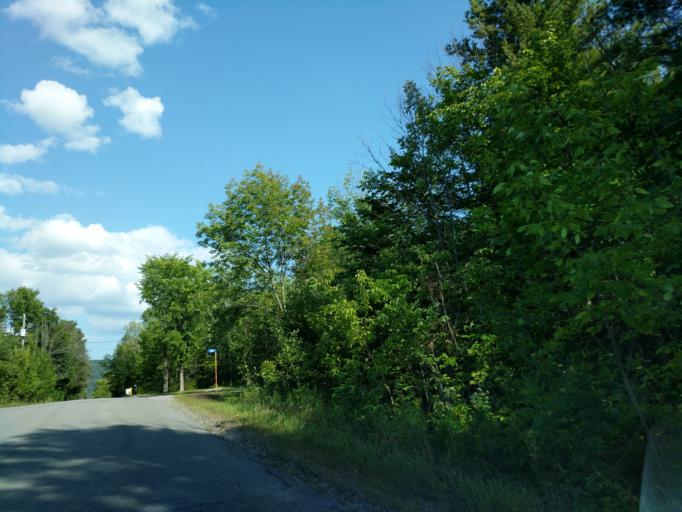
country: CA
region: Quebec
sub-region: Outaouais
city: Wakefield
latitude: 45.5032
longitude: -75.9507
